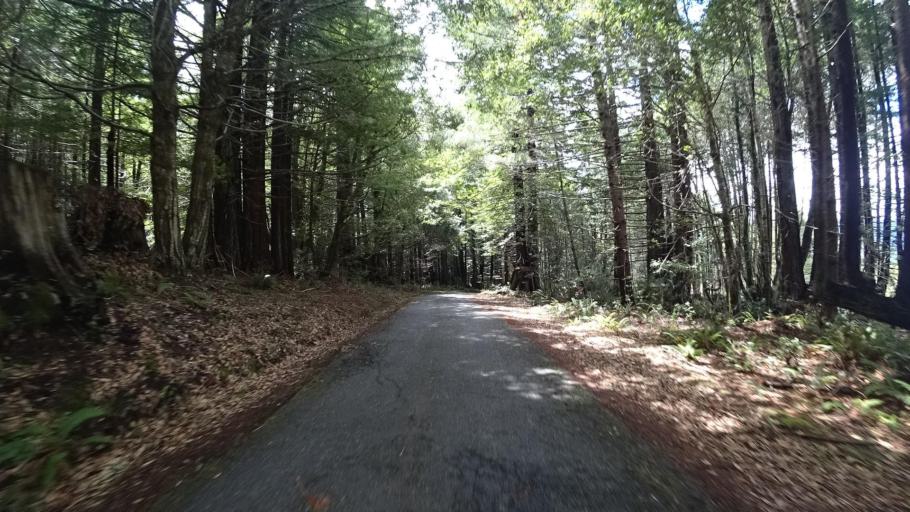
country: US
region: California
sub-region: Humboldt County
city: Blue Lake
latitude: 40.7828
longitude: -123.9626
